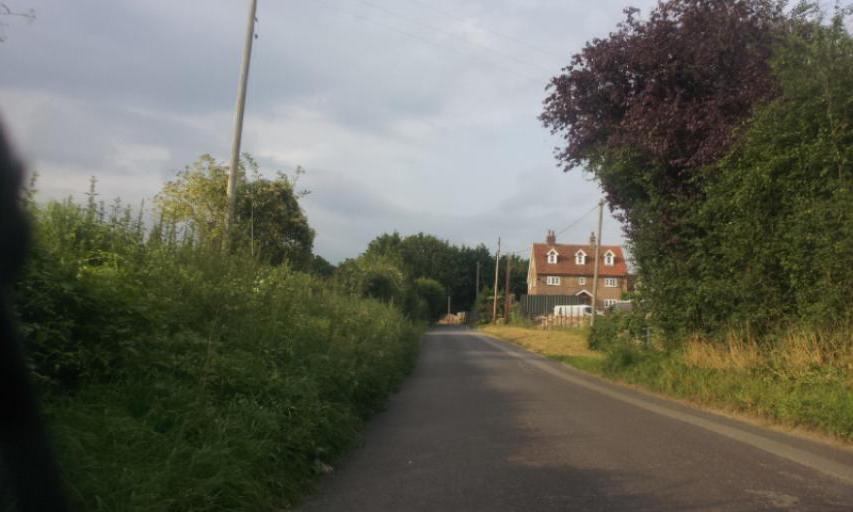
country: GB
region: England
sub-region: Kent
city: Yalding
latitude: 51.2347
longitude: 0.4236
